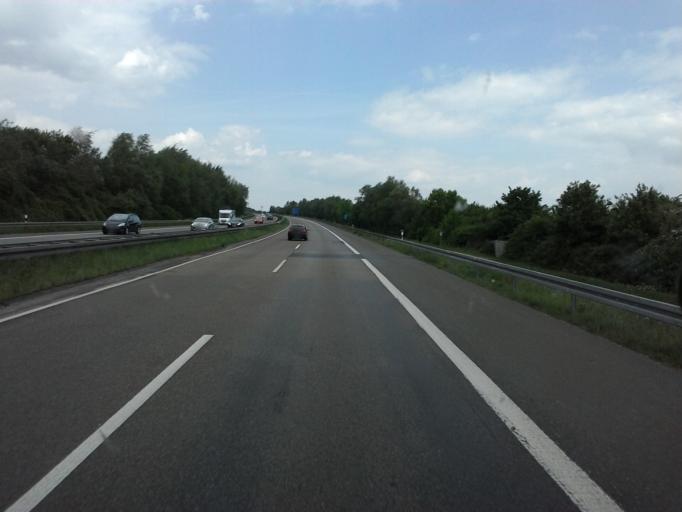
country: DE
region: North Rhine-Westphalia
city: Rheinberg
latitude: 51.5200
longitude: 6.5858
